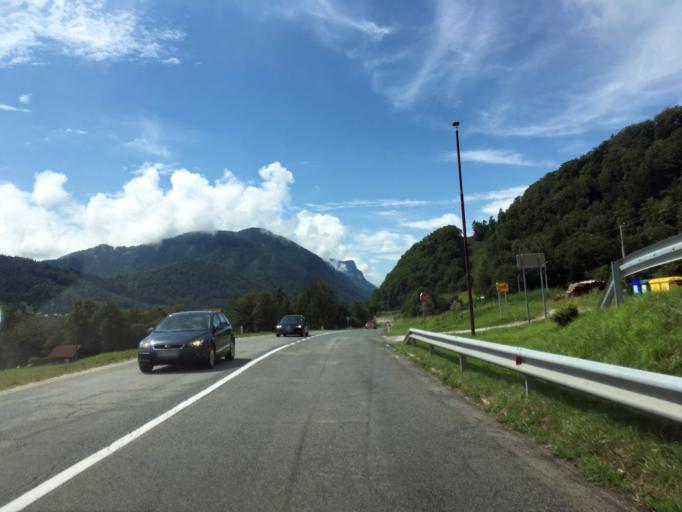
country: SI
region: Bled
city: Zasip
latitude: 46.4155
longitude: 14.1177
